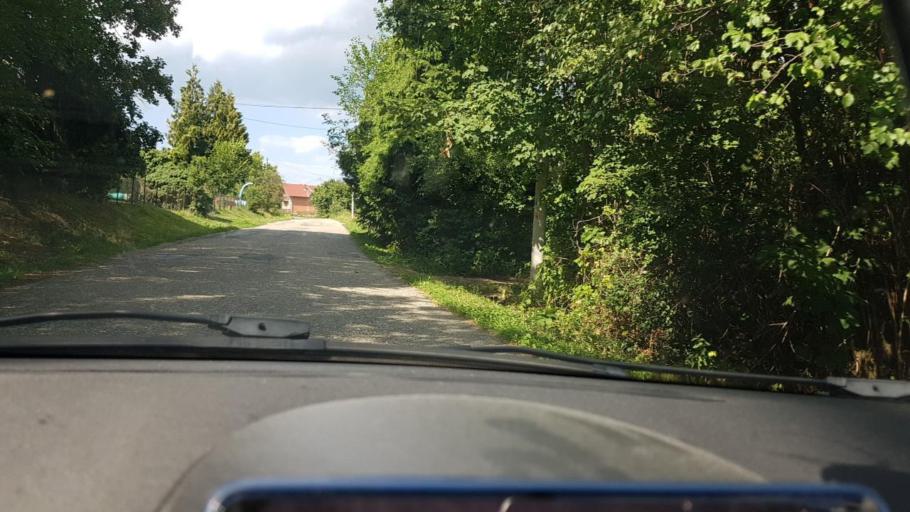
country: HR
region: Bjelovarsko-Bilogorska
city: Zdralovi
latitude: 45.8745
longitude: 17.0007
